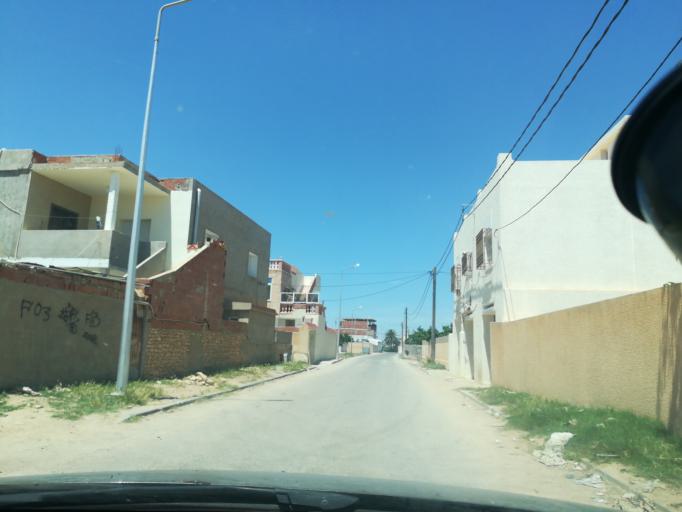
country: TN
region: Safaqis
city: Al Qarmadah
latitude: 34.8187
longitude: 10.7553
